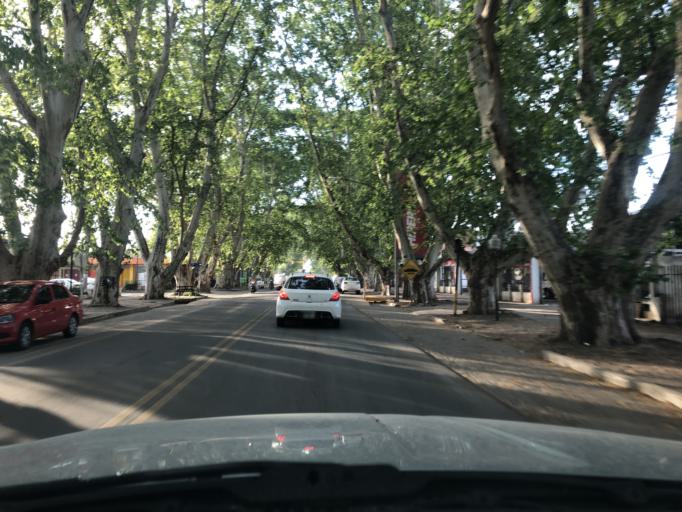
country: AR
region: Cordoba
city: Jesus Maria
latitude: -30.9919
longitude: -64.0961
